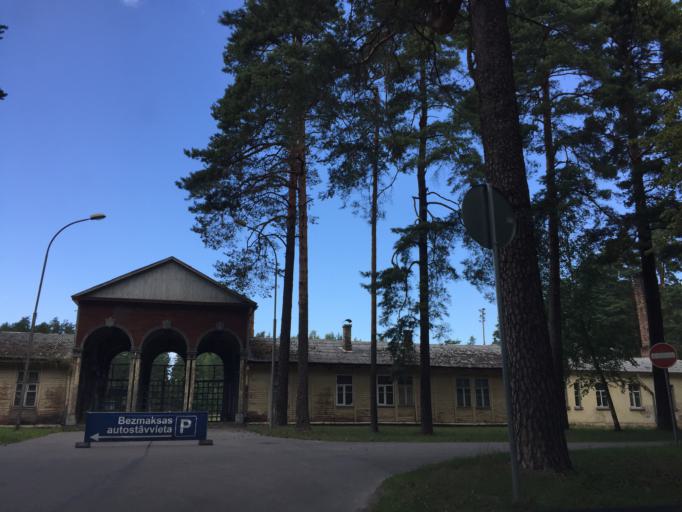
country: LV
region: Riga
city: Jaunciems
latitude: 57.0034
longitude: 24.1500
